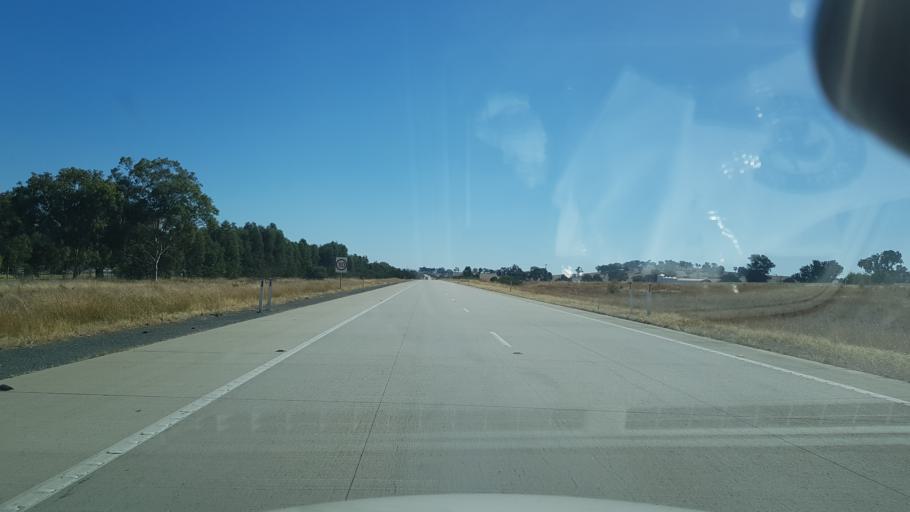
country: AU
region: New South Wales
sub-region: Albury Municipality
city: Lavington
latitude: -35.9270
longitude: 147.0763
